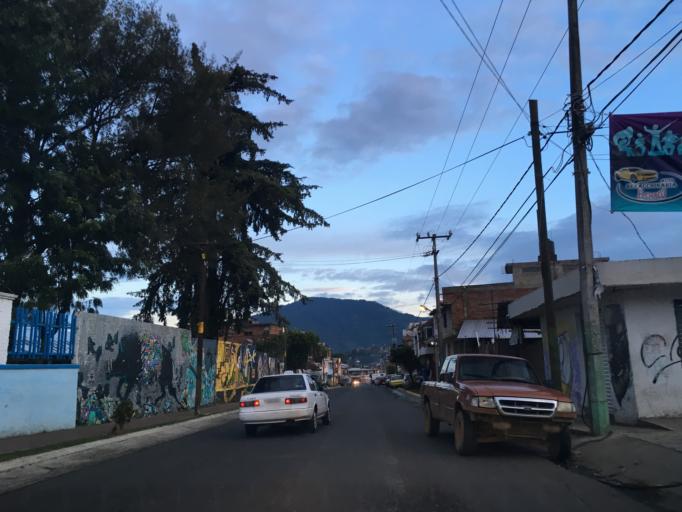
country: MX
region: Michoacan
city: Cheran
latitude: 19.6802
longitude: -101.9543
